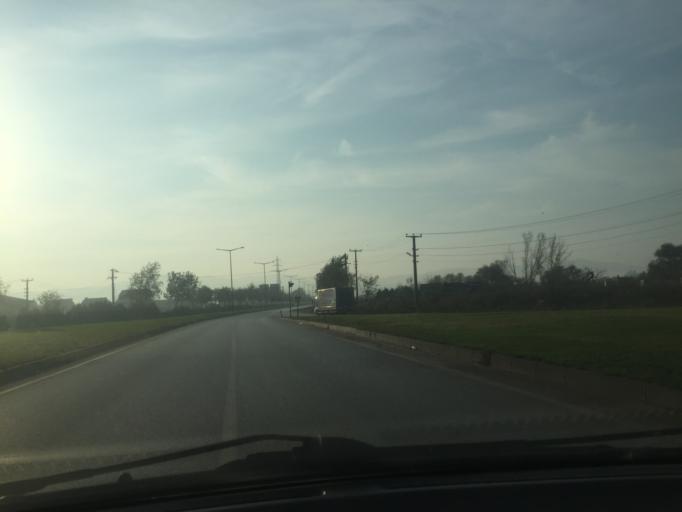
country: TR
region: Canakkale
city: Biga
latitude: 40.2405
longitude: 27.2570
